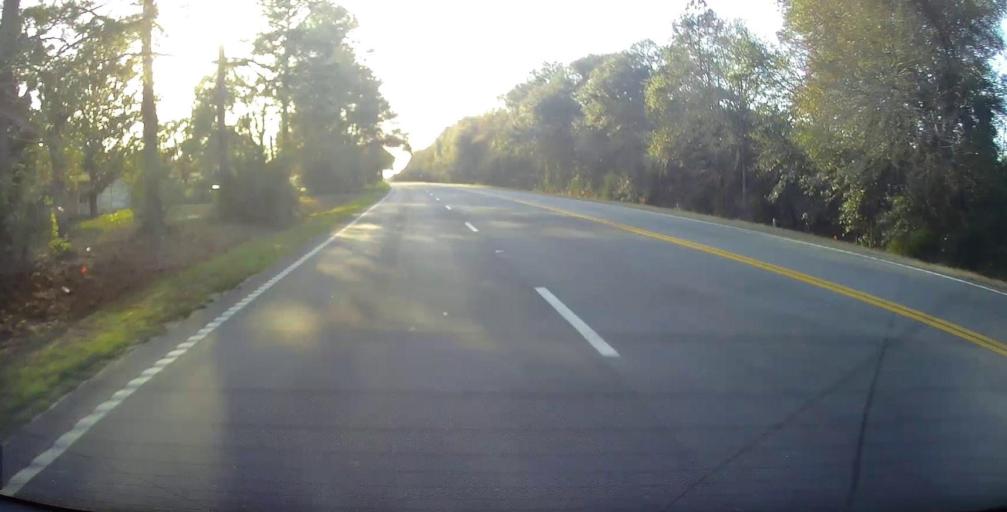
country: US
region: Georgia
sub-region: Evans County
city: Claxton
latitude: 32.1525
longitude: -81.8072
